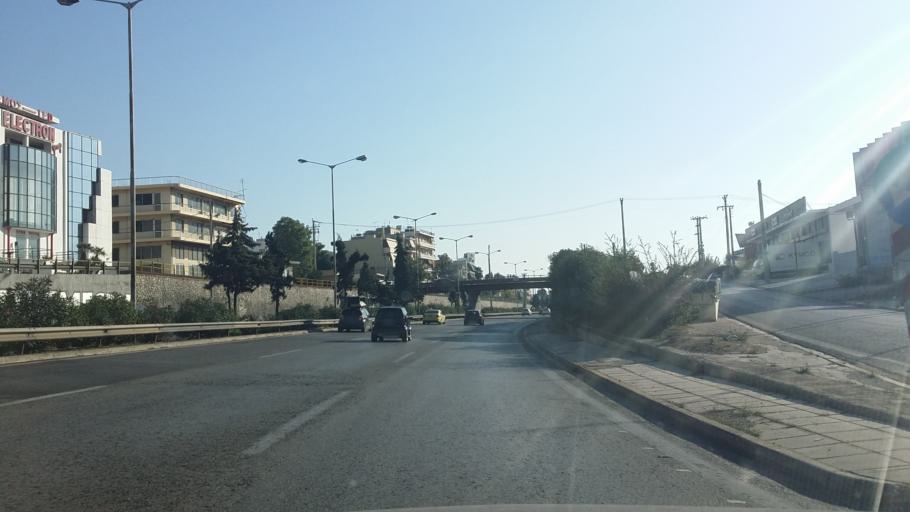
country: GR
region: Attica
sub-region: Nomarchia Athinas
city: Nea Filadelfeia
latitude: 38.0385
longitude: 23.7337
